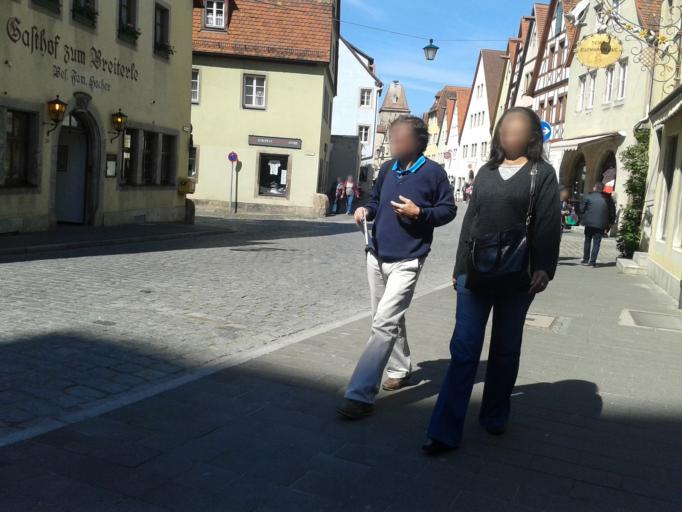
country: DE
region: Bavaria
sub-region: Regierungsbezirk Mittelfranken
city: Rothenburg ob der Tauber
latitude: 49.3770
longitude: 10.1836
